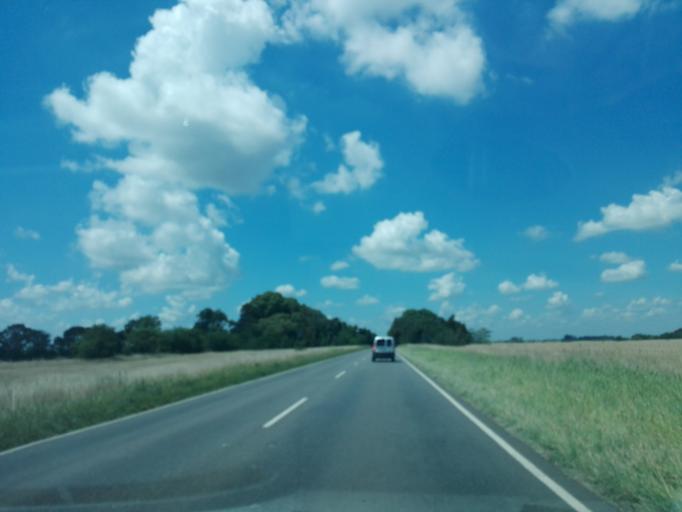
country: AR
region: Buenos Aires
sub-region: Partido de General Belgrano
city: General Belgrano
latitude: -35.8738
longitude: -58.6180
